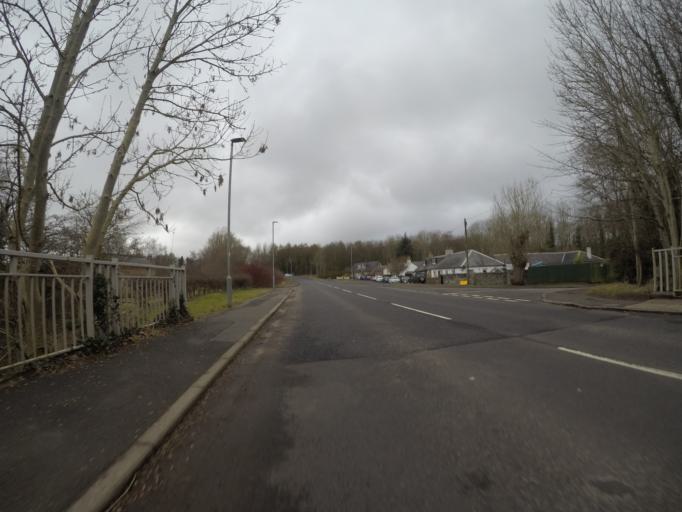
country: GB
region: Scotland
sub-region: North Ayrshire
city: Springside
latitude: 55.6308
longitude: -4.6218
